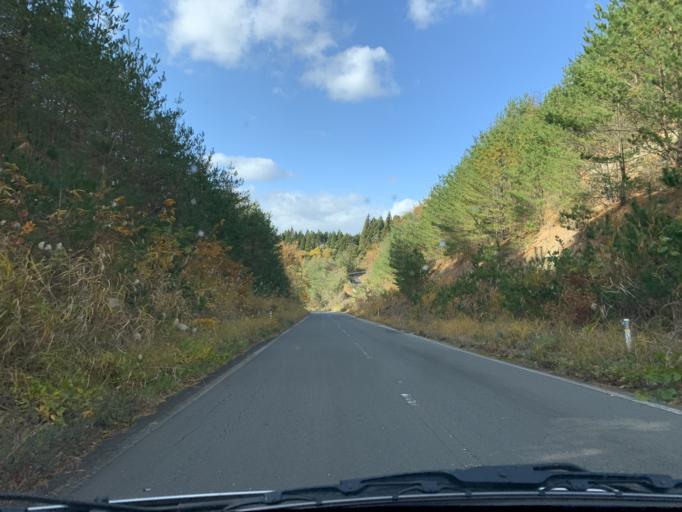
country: JP
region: Iwate
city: Mizusawa
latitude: 39.0352
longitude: 141.0806
